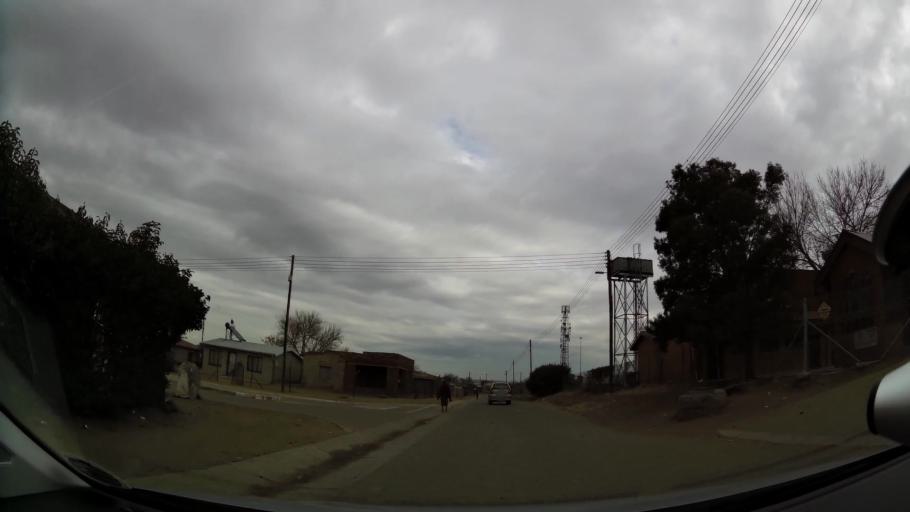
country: ZA
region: Orange Free State
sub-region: Fezile Dabi District Municipality
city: Kroonstad
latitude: -27.6489
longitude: 27.2042
